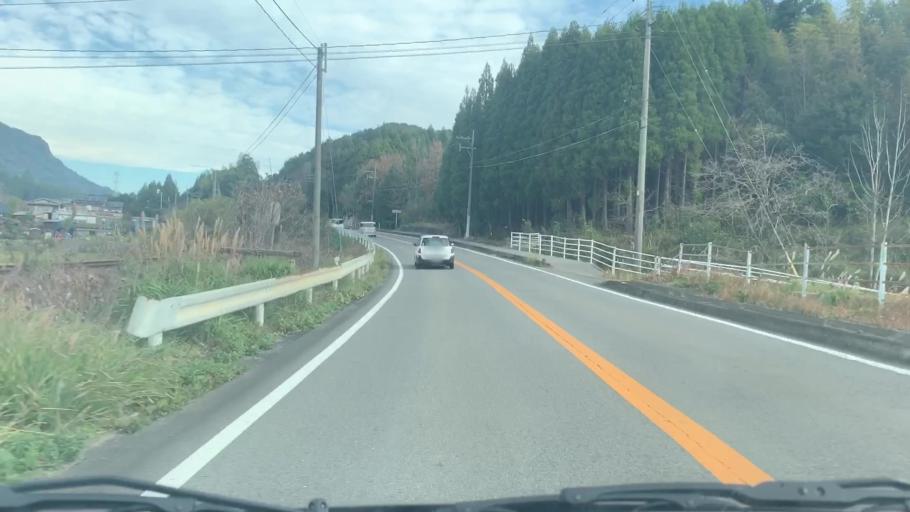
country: JP
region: Saga Prefecture
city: Karatsu
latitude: 33.3388
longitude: 129.9799
